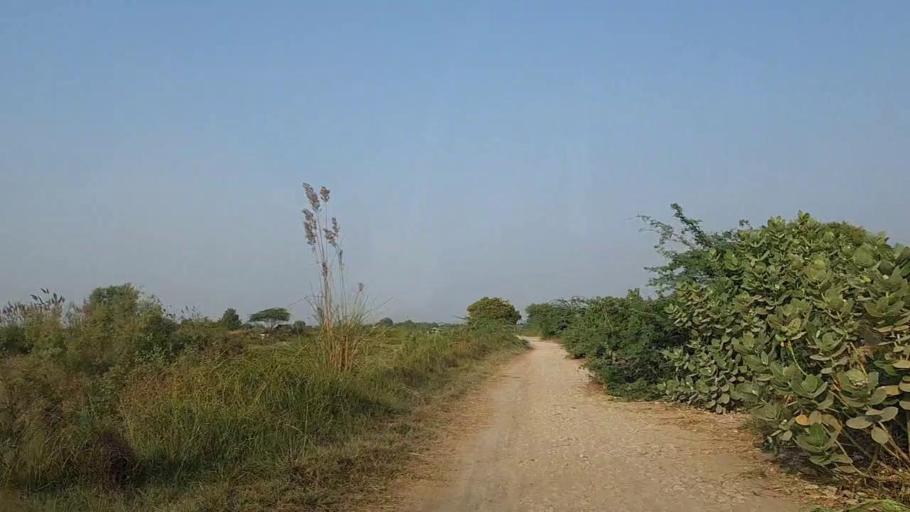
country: PK
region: Sindh
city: Thatta
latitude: 24.6654
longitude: 67.7785
